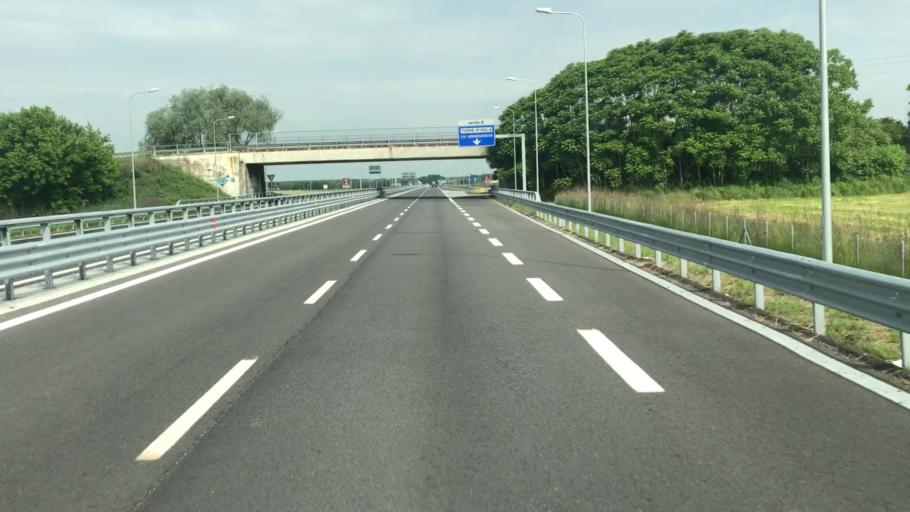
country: IT
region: Lombardy
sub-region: Provincia di Pavia
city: Torre d'Isola
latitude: 45.2204
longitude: 9.0840
